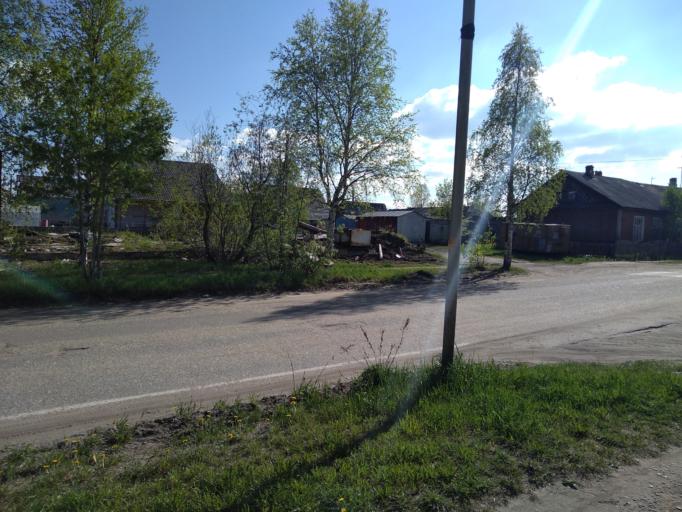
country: RU
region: Komi Republic
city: Pechora
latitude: 65.1143
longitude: 57.1502
